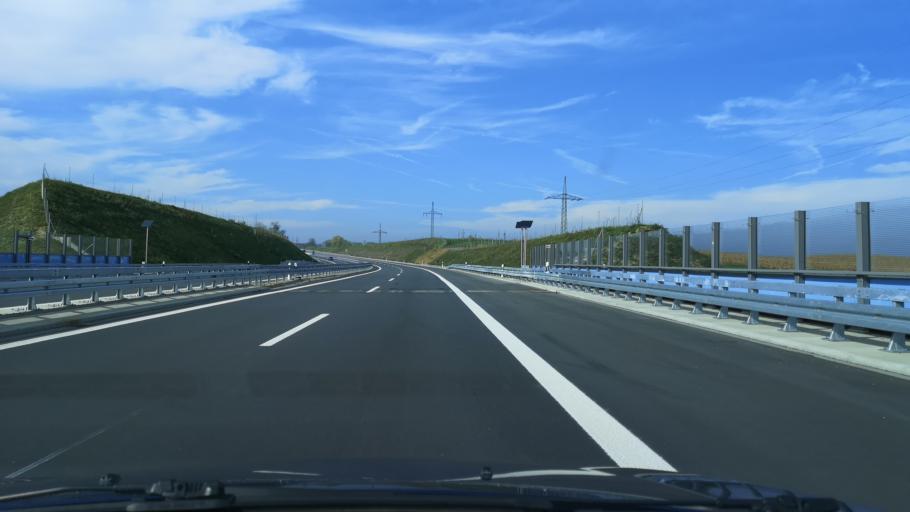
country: DE
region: Bavaria
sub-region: Upper Bavaria
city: Dorfen
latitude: 48.2555
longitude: 12.1307
